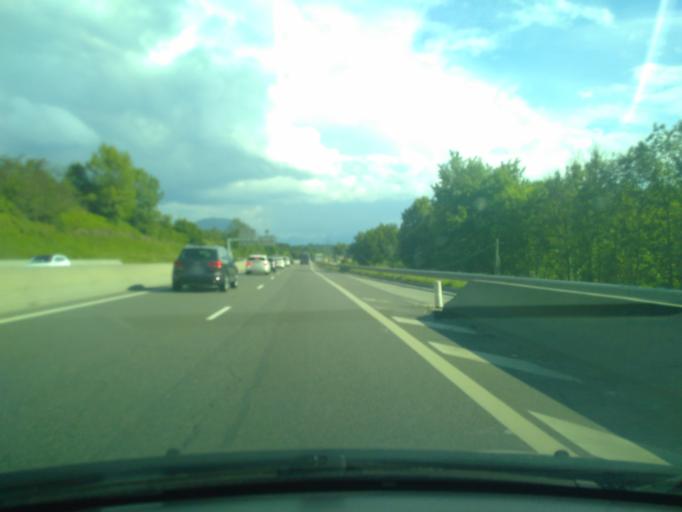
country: FR
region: Rhone-Alpes
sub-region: Departement de la Haute-Savoie
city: Allonzier-la-Caille
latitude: 45.9836
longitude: 6.1290
